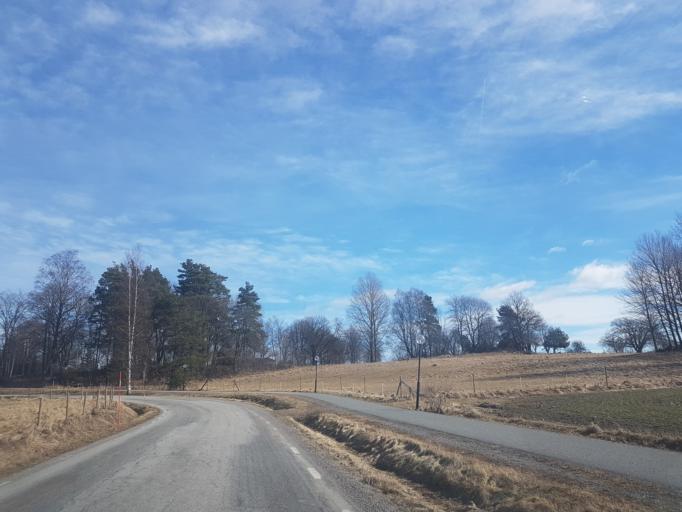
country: SE
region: Stockholm
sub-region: Norrtalje Kommun
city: Rimbo
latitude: 59.7487
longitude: 18.3858
